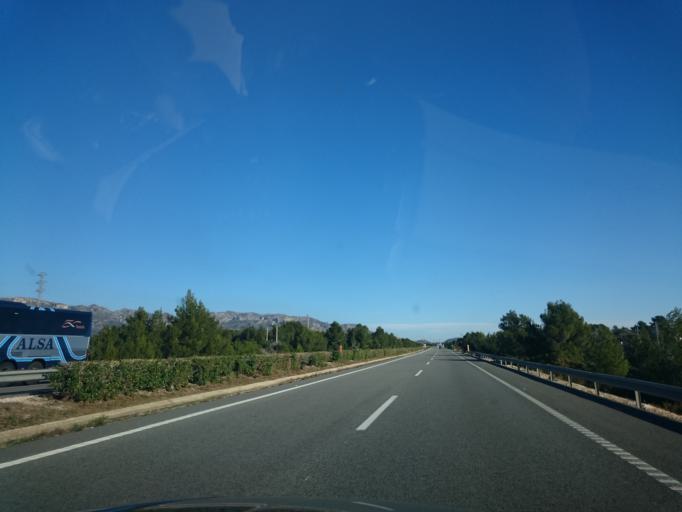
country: ES
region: Catalonia
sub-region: Provincia de Tarragona
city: l'Ametlla de Mar
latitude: 40.9135
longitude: 0.8261
